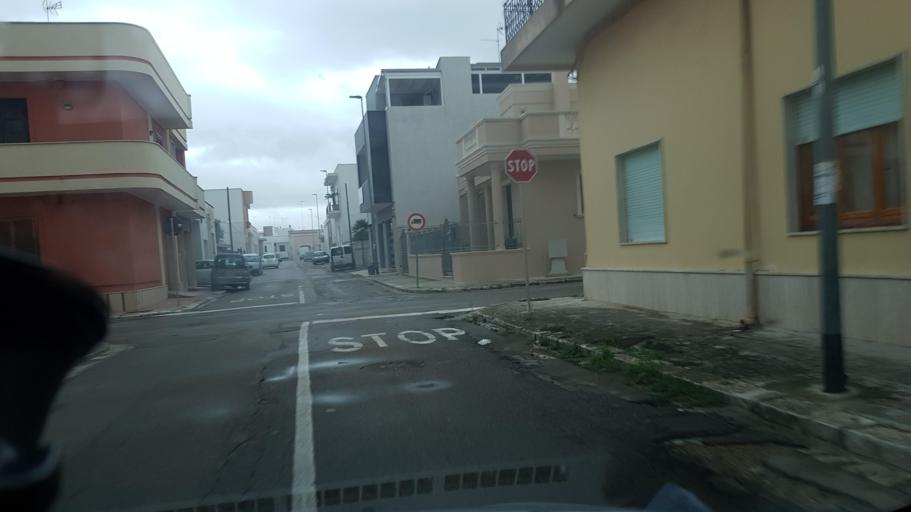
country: IT
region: Apulia
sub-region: Provincia di Lecce
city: Carmiano
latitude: 40.3417
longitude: 18.0447
